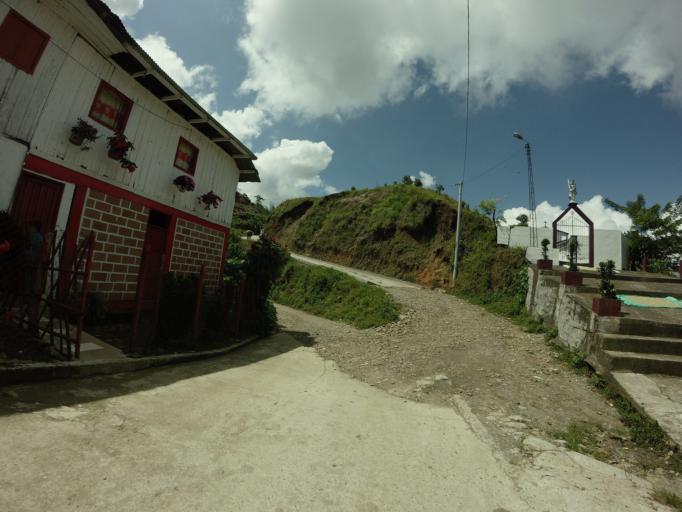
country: CO
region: Antioquia
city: Narino
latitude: 5.4980
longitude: -75.1856
